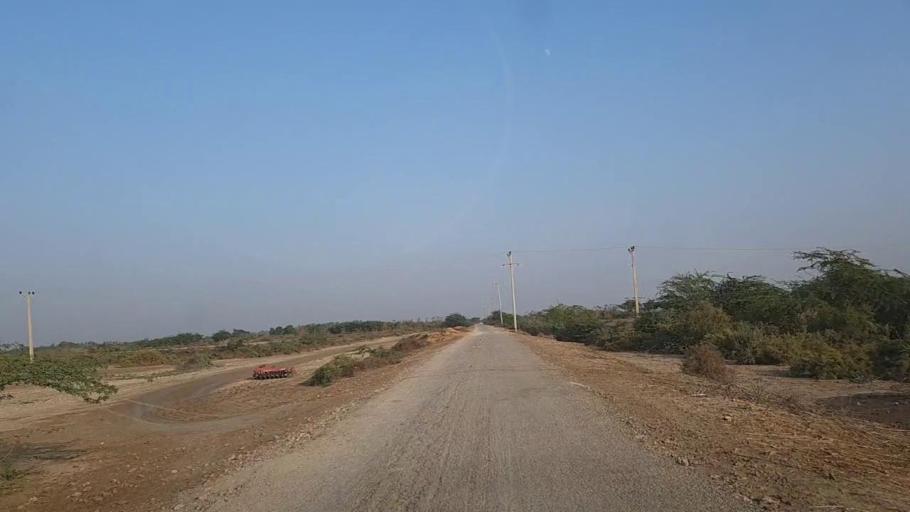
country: PK
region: Sindh
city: Keti Bandar
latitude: 24.2805
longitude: 67.6154
